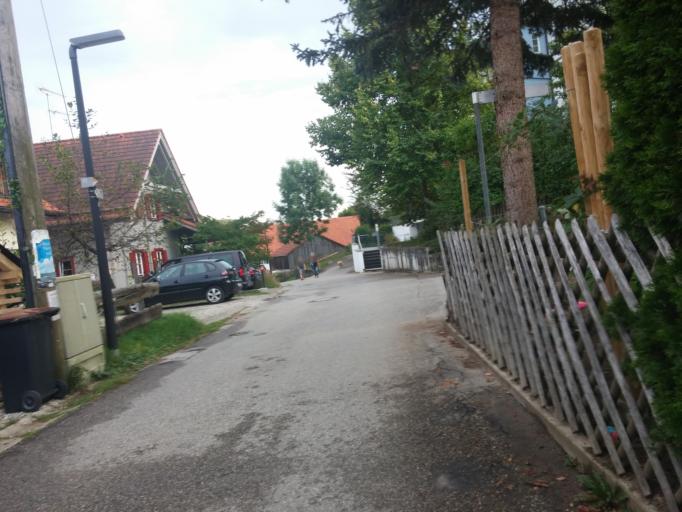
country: DE
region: Bavaria
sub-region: Upper Bavaria
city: Schondorf am Ammersee
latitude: 48.0525
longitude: 11.0858
